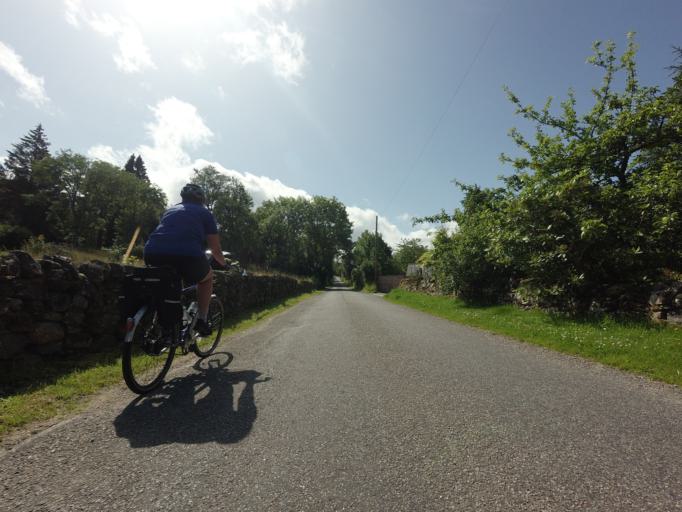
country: GB
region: Scotland
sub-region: Highland
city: Nairn
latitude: 57.5022
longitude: -3.9980
